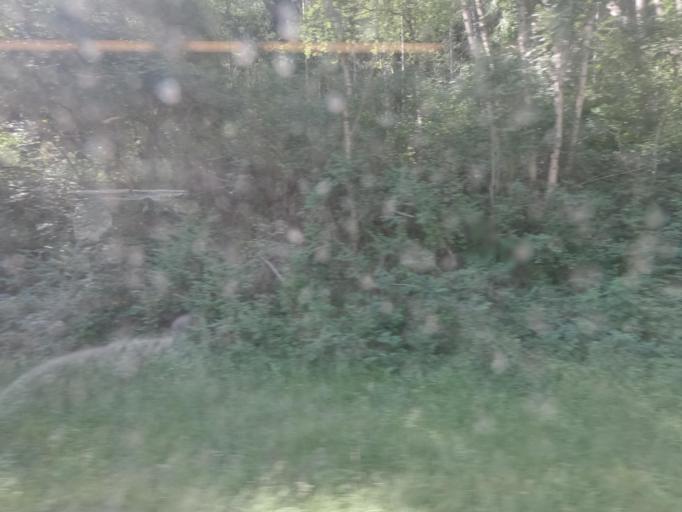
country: CH
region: Valais
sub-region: Martigny District
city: Charrat-les-Chenes
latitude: 46.0779
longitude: 7.1309
